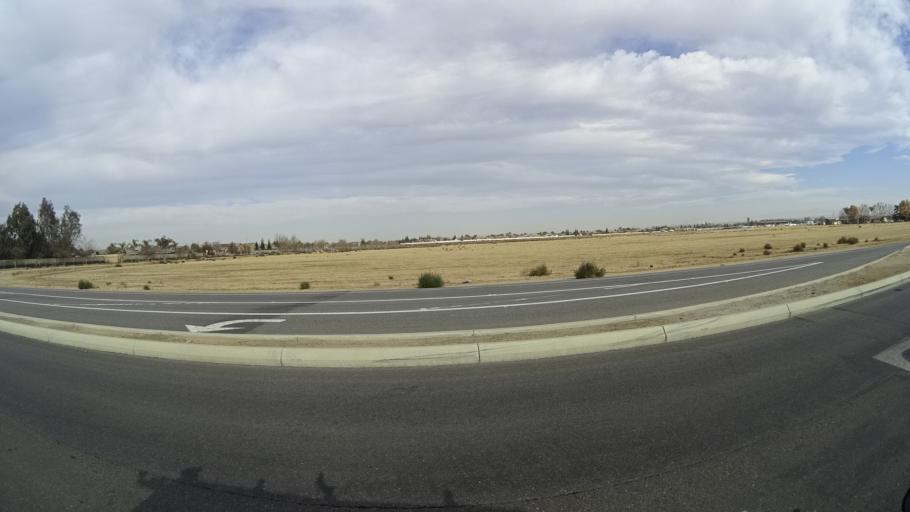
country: US
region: California
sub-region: Kern County
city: Greenacres
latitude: 35.4269
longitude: -119.1181
